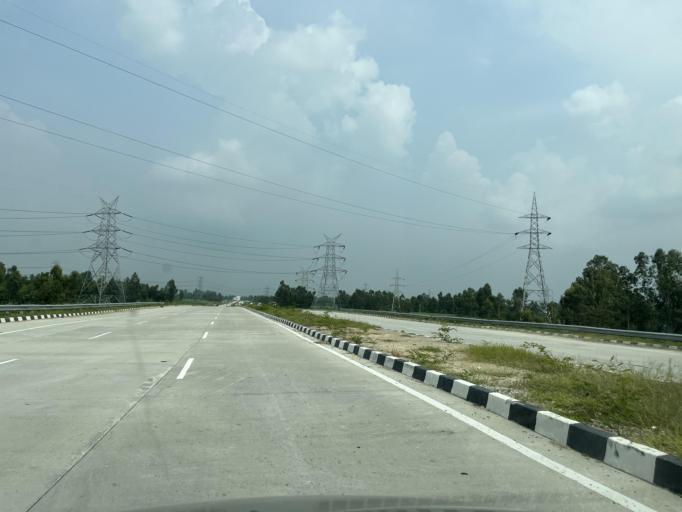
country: IN
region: Uttarakhand
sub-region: Udham Singh Nagar
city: Jaspur
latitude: 29.2969
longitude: 78.8210
